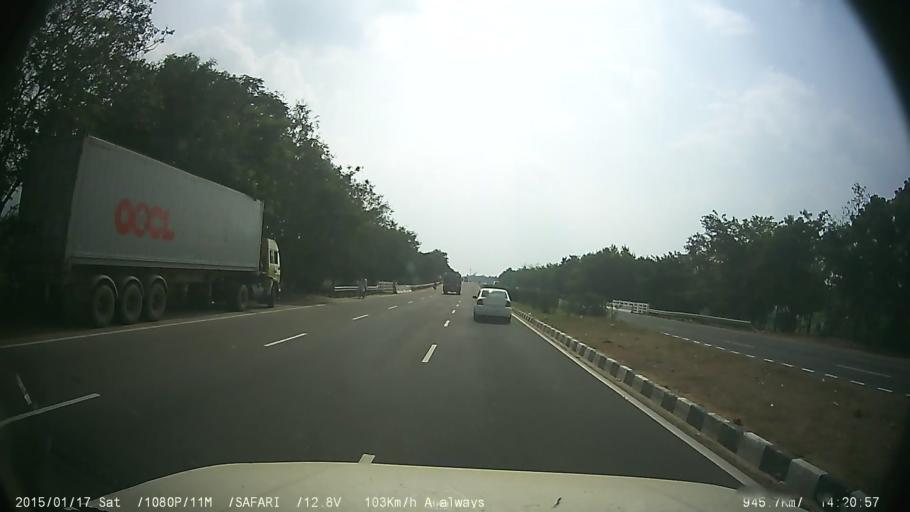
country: IN
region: Tamil Nadu
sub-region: Vellore
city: Vaniyambadi
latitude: 12.7028
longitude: 78.6457
